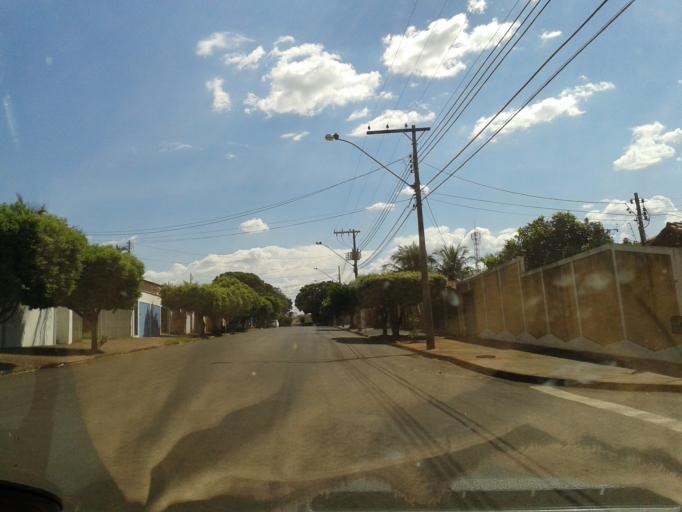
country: BR
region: Minas Gerais
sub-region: Ituiutaba
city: Ituiutaba
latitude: -18.9863
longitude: -49.4556
